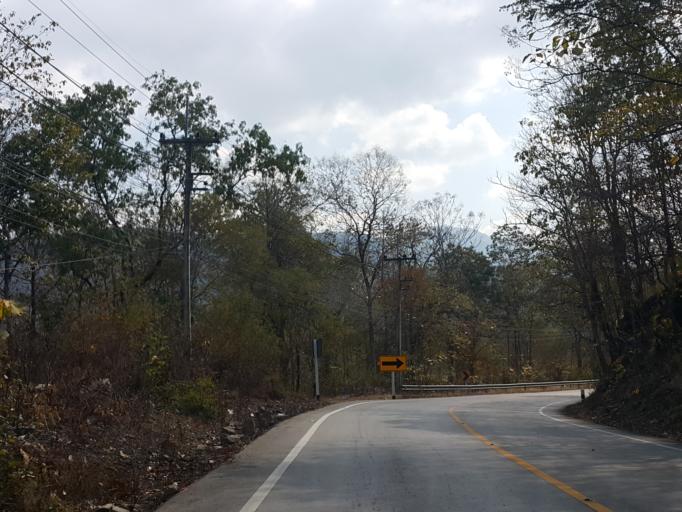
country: TH
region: Chiang Mai
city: Hot
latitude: 18.2076
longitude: 98.4482
